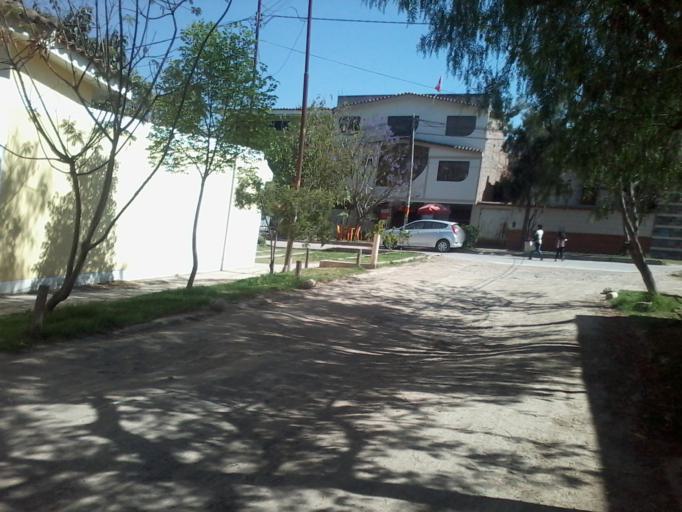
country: PE
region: Ayacucho
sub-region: Provincia de Huamanga
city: Ayacucho
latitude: -13.1627
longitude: -74.2118
